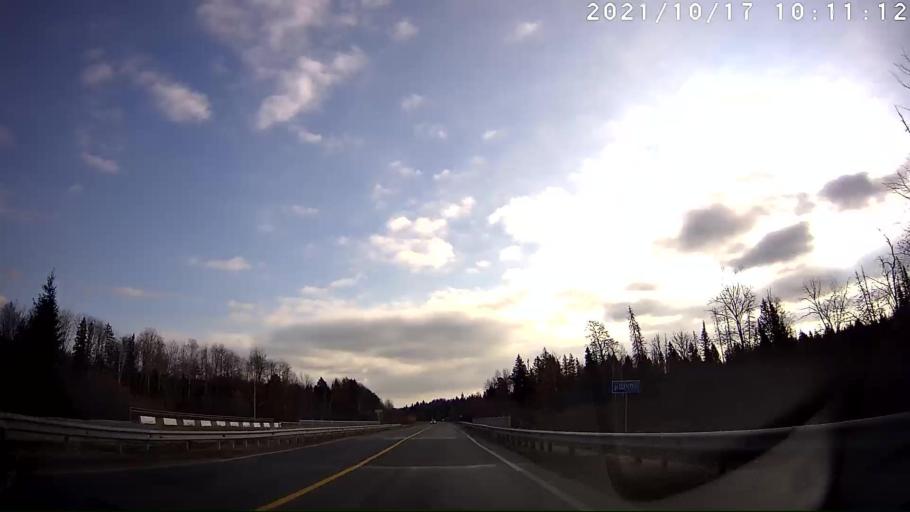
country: RU
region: Mariy-El
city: Sovetskiy
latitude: 56.7395
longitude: 48.3858
